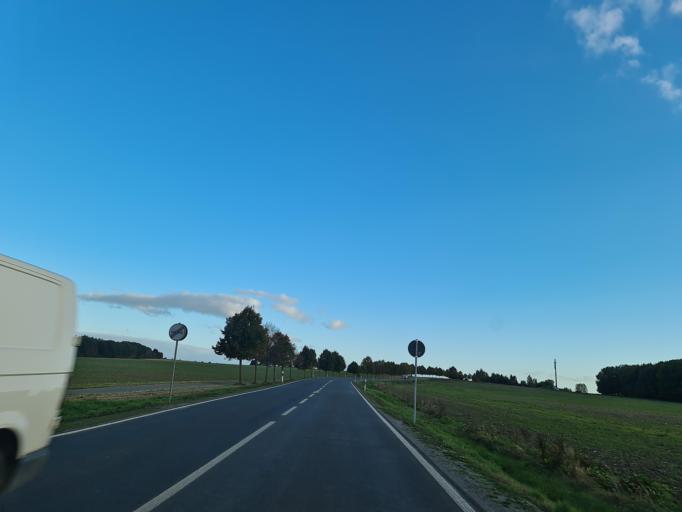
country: DE
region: Thuringia
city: Wildetaube
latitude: 50.7269
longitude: 12.1065
